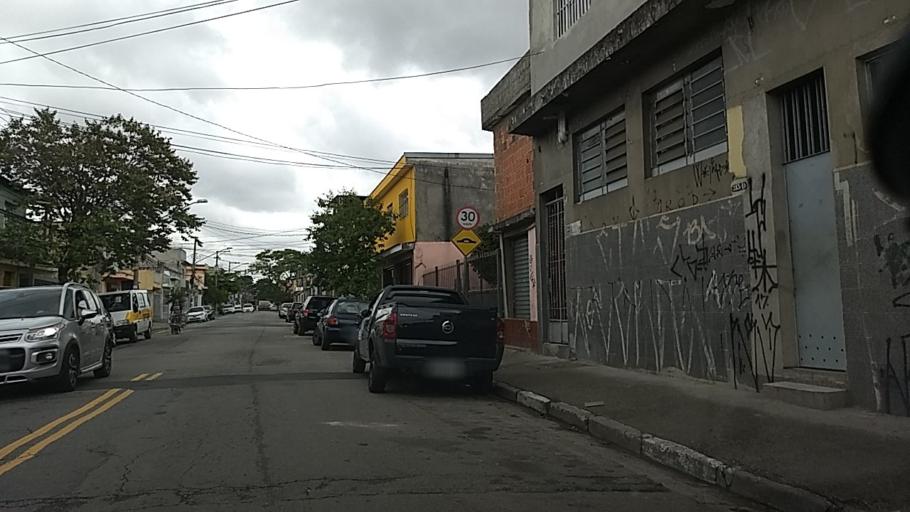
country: BR
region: Sao Paulo
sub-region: Guarulhos
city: Guarulhos
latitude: -23.4896
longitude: -46.5698
